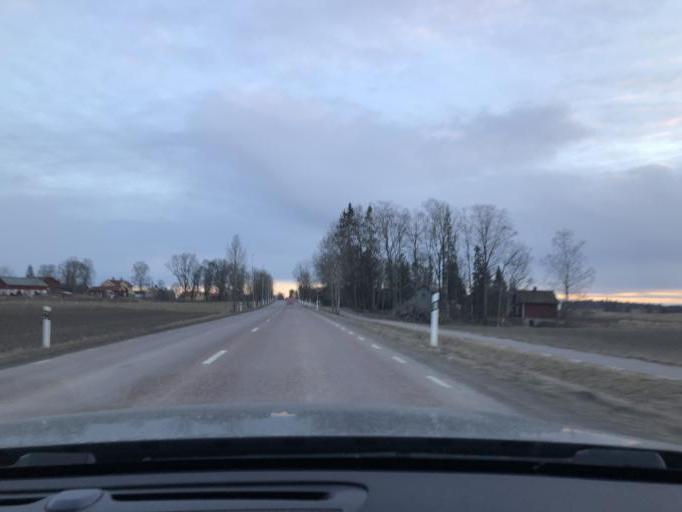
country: SE
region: Uppsala
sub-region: Uppsala Kommun
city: Gamla Uppsala
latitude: 59.9163
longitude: 17.6426
